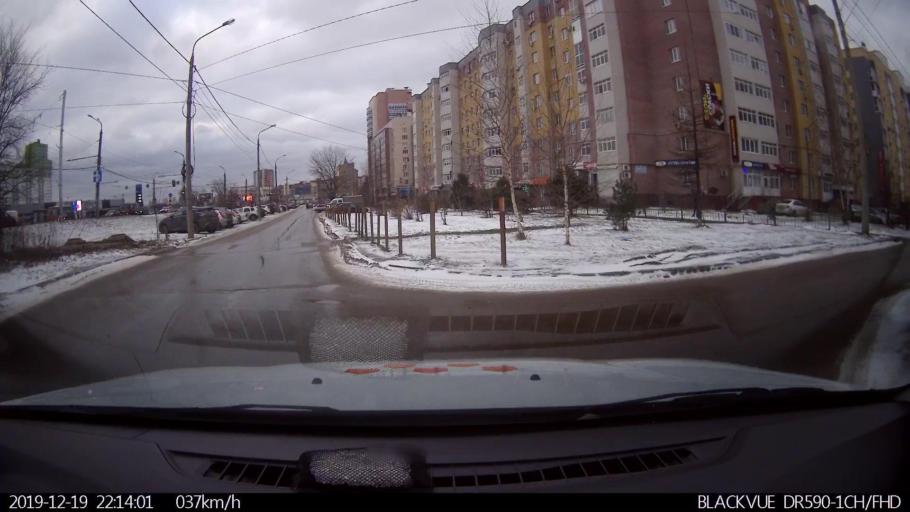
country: RU
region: Nizjnij Novgorod
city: Afonino
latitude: 56.3013
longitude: 44.0789
